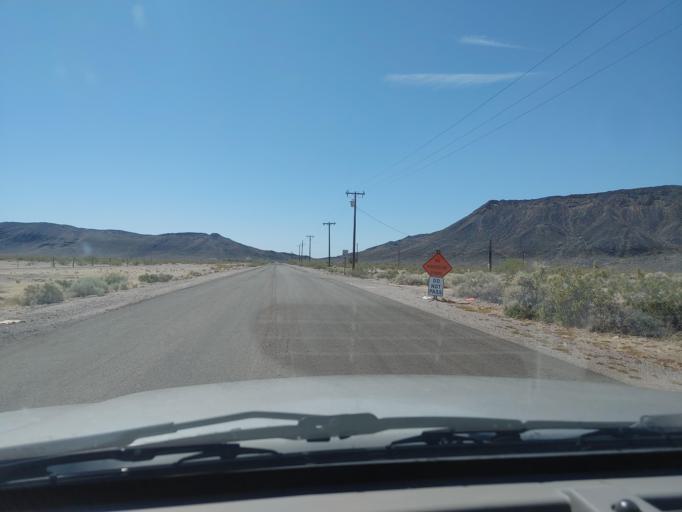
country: US
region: Arizona
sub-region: Maricopa County
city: Gila Bend
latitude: 33.0201
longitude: -113.3405
